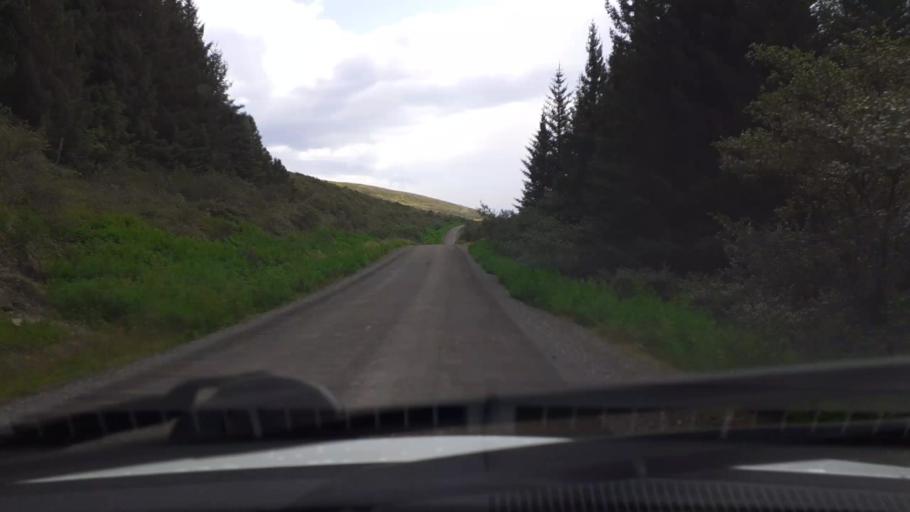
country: IS
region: Capital Region
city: Mosfellsbaer
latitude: 64.5278
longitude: -21.5012
